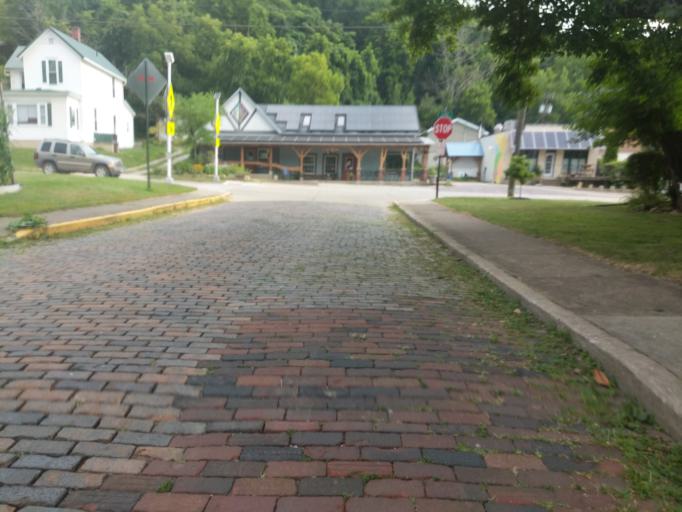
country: US
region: Ohio
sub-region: Athens County
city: Athens
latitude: 39.3371
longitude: -82.0922
